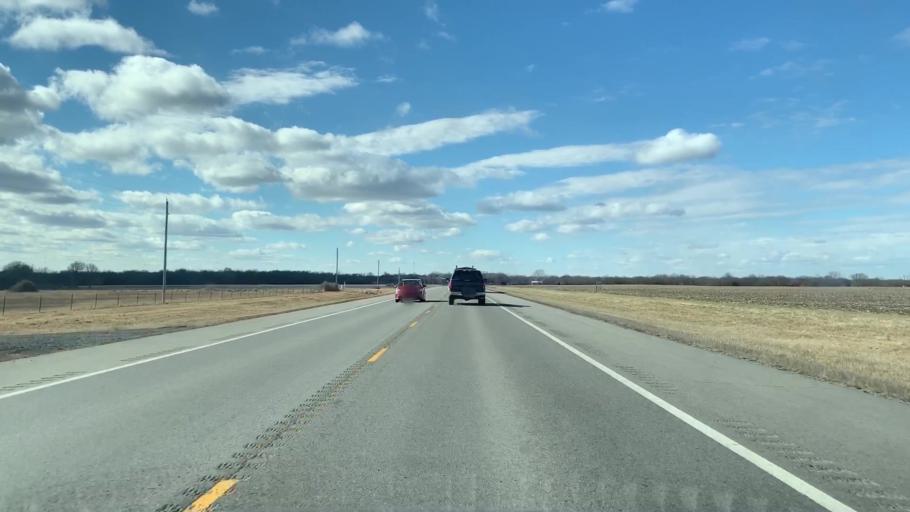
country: US
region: Kansas
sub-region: Cherokee County
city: Columbus
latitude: 37.3398
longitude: -94.8717
